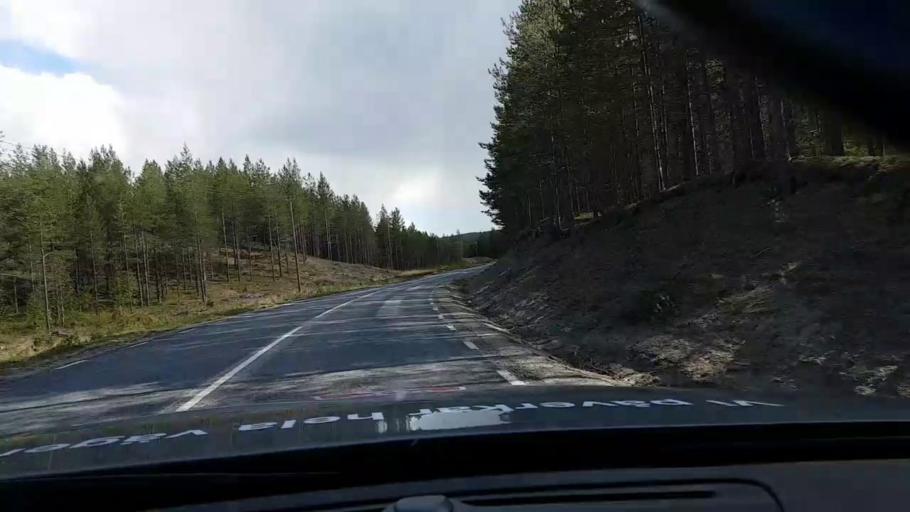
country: SE
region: Vaesterbotten
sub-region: Asele Kommun
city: Asele
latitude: 63.8539
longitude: 17.3912
